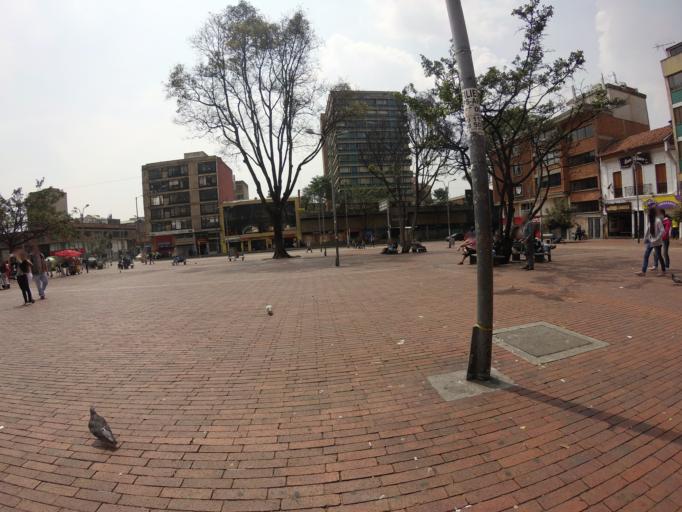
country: CO
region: Bogota D.C.
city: Bogota
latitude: 4.6498
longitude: -74.0630
